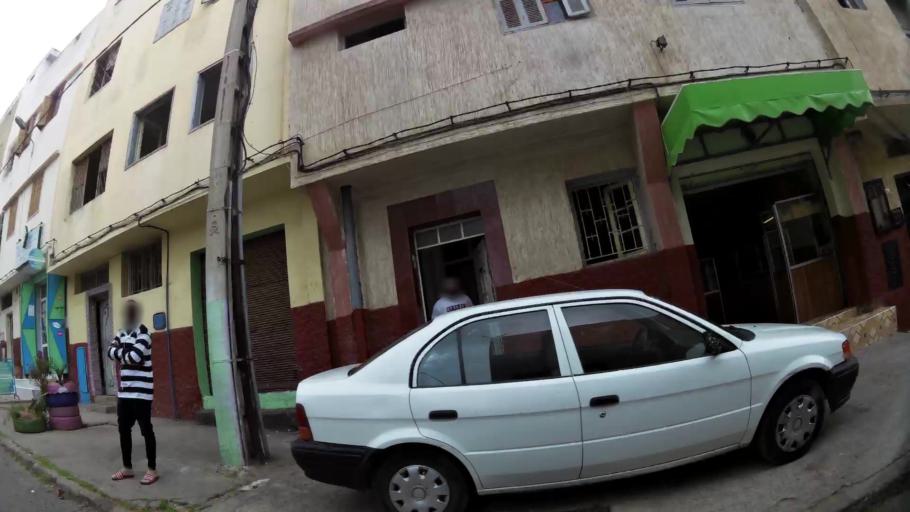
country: MA
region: Rabat-Sale-Zemmour-Zaer
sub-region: Rabat
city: Rabat
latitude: 33.9983
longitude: -6.8185
